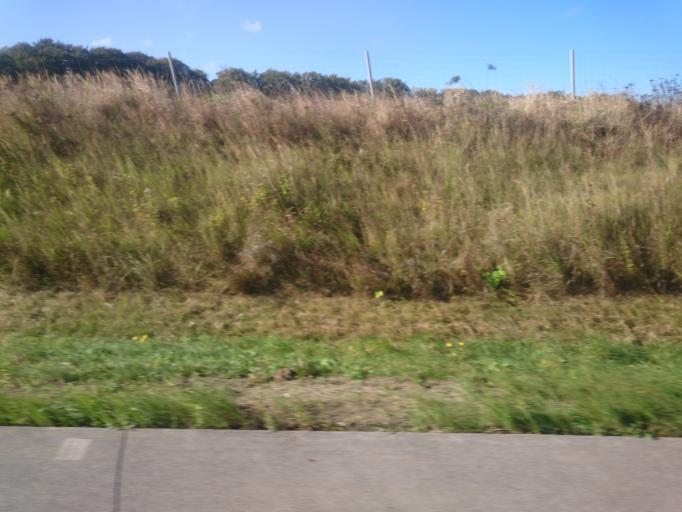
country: DE
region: Mecklenburg-Vorpommern
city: Laage
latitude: 53.9066
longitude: 12.2440
